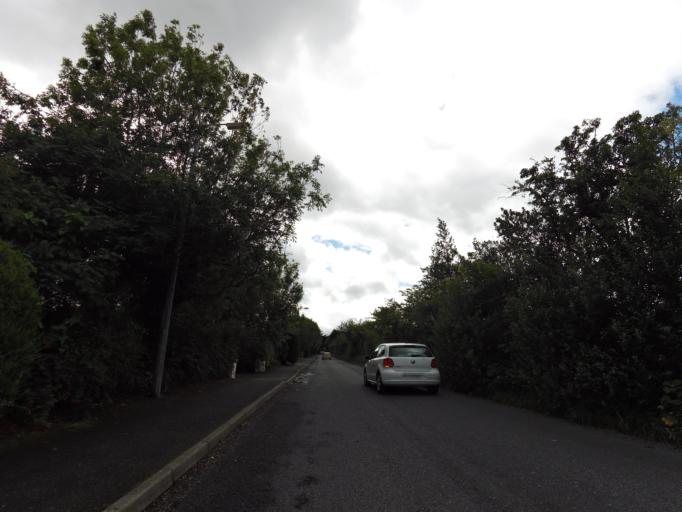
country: IE
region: Connaught
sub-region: County Galway
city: Oughterard
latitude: 53.4245
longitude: -9.3277
